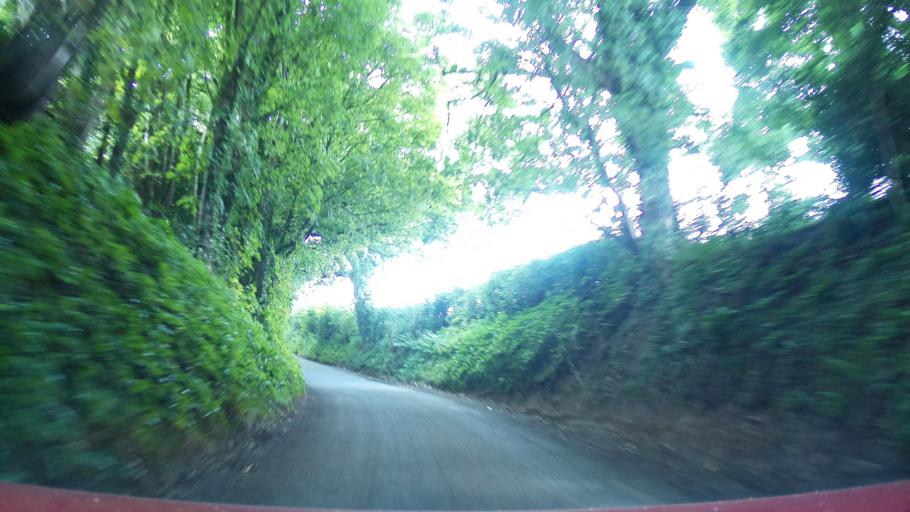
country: GB
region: England
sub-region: Somerset
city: Chilcompton
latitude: 51.2177
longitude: -2.4996
